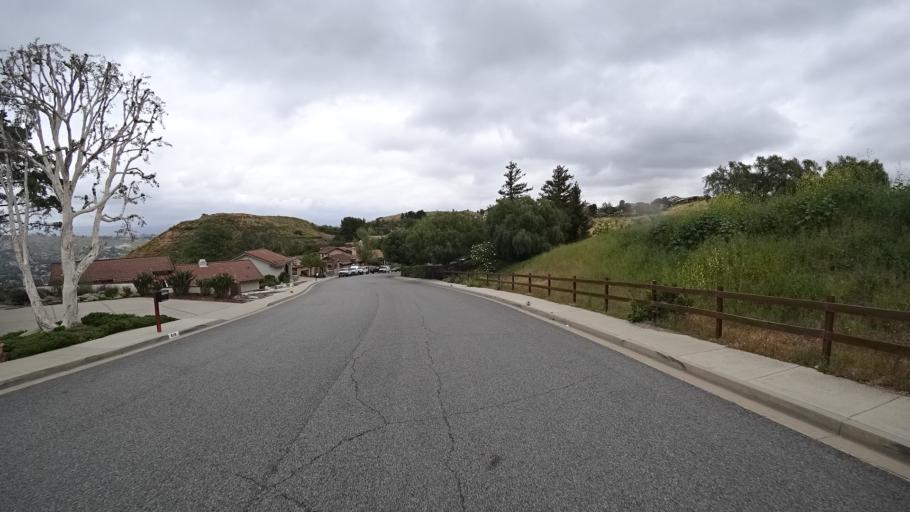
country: US
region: California
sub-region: Ventura County
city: Moorpark
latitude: 34.2279
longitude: -118.8966
